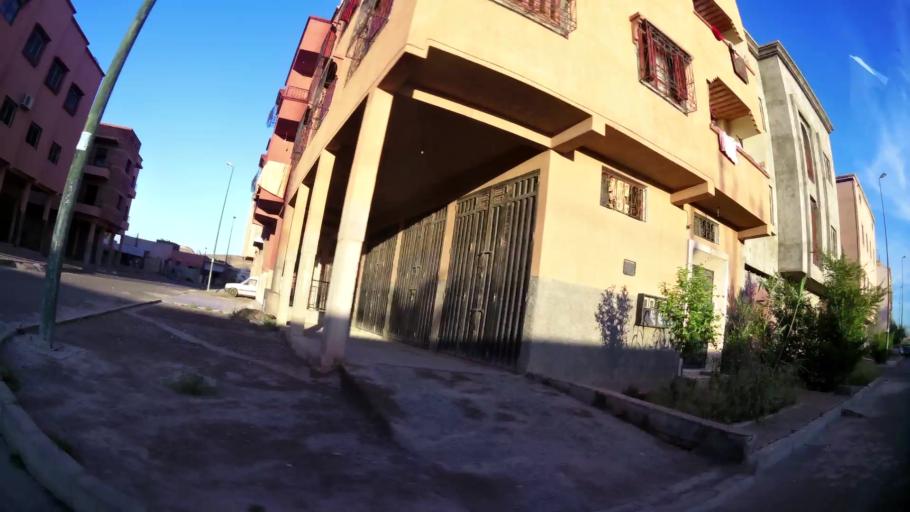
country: MA
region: Marrakech-Tensift-Al Haouz
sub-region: Marrakech
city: Marrakesh
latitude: 31.6422
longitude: -8.0405
